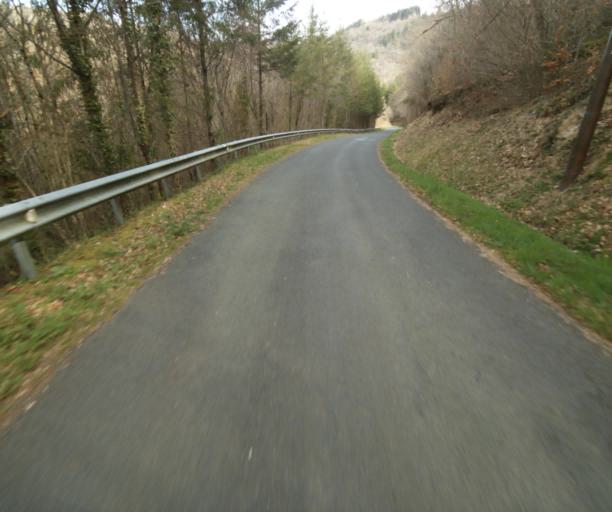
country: FR
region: Limousin
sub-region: Departement de la Correze
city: Correze
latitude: 45.4249
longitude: 1.8013
